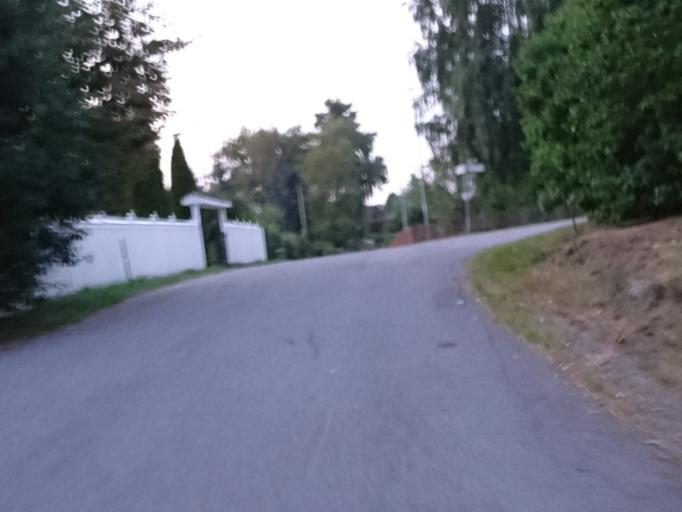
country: SE
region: Stockholm
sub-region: Huddinge Kommun
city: Segeltorp
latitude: 59.2794
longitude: 17.9334
